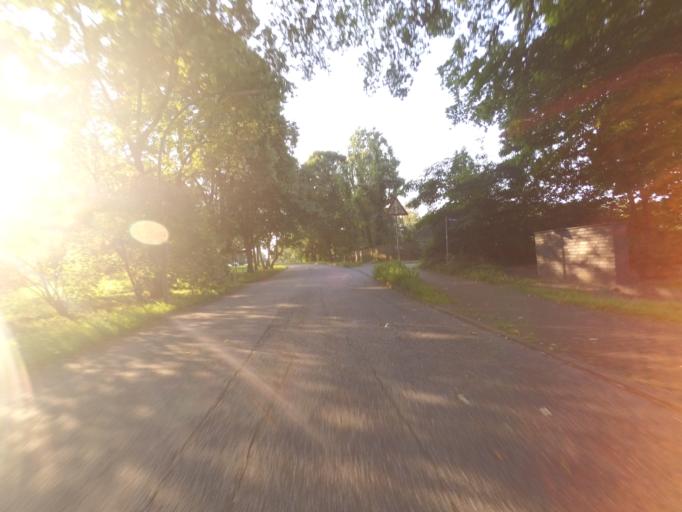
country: DE
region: Schleswig-Holstein
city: Oststeinbek
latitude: 53.5104
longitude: 10.1732
